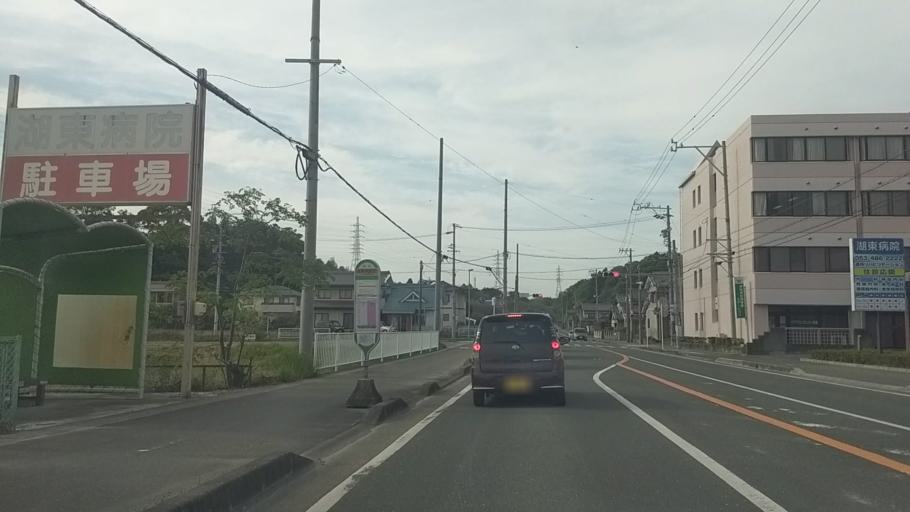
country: JP
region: Shizuoka
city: Hamamatsu
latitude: 34.7463
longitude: 137.6546
